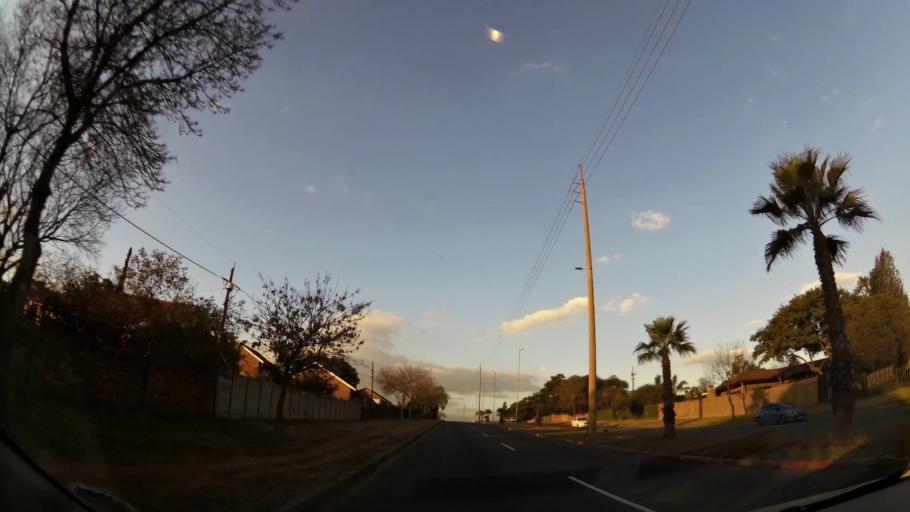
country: ZA
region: Gauteng
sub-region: West Rand District Municipality
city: Krugersdorp
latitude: -26.0784
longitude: 27.7763
